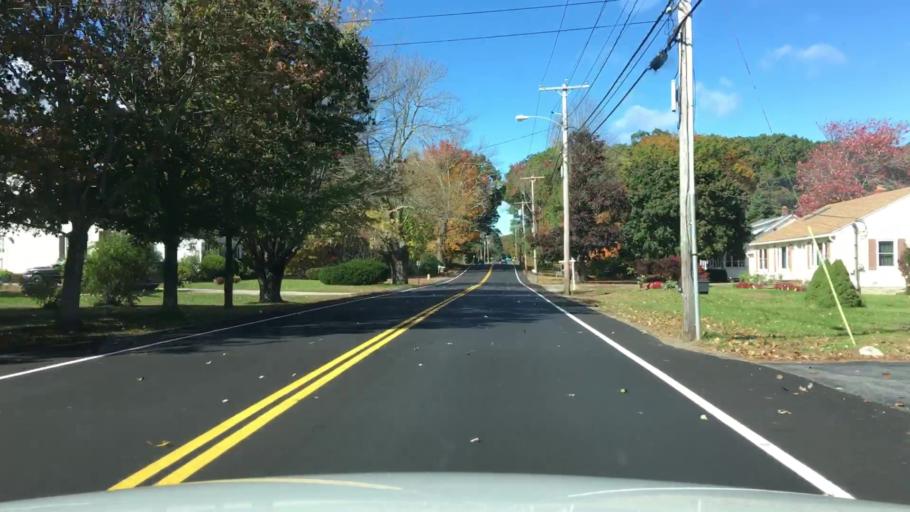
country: US
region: Maine
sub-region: York County
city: Biddeford
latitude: 43.4573
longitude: -70.4316
